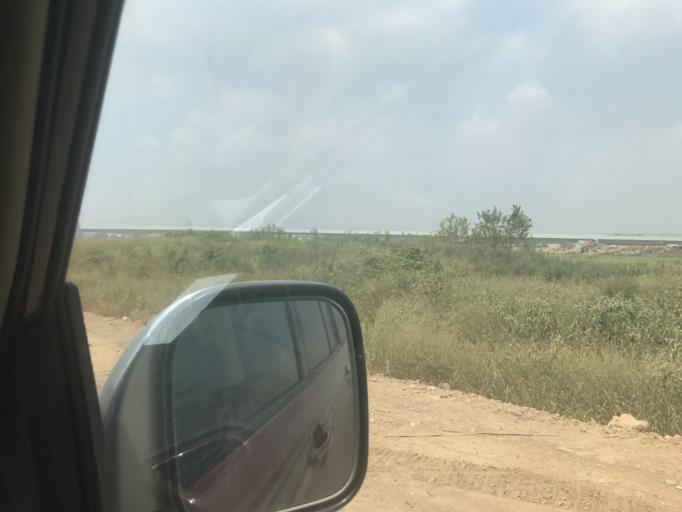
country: CN
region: Hubei
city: Zhanjiaji
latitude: 30.6838
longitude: 114.3408
